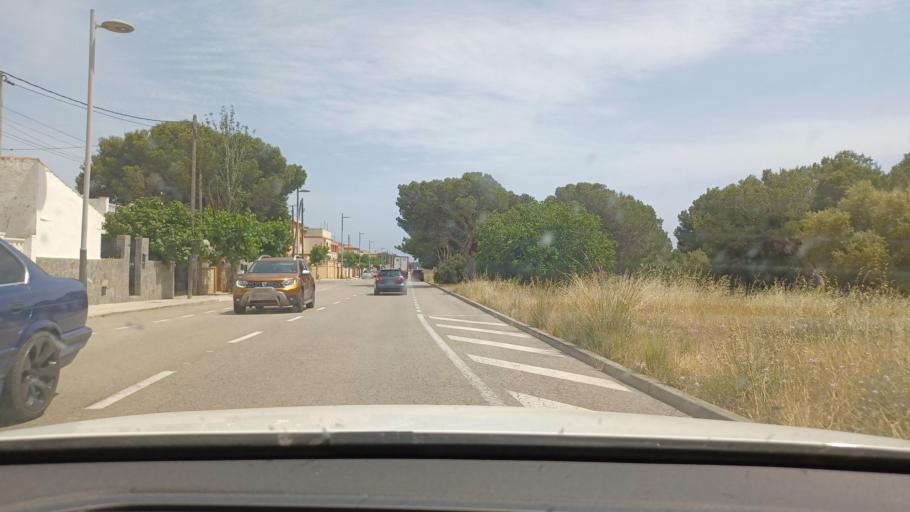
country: ES
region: Catalonia
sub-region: Provincia de Tarragona
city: Colldejou
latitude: 41.0035
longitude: 0.9256
